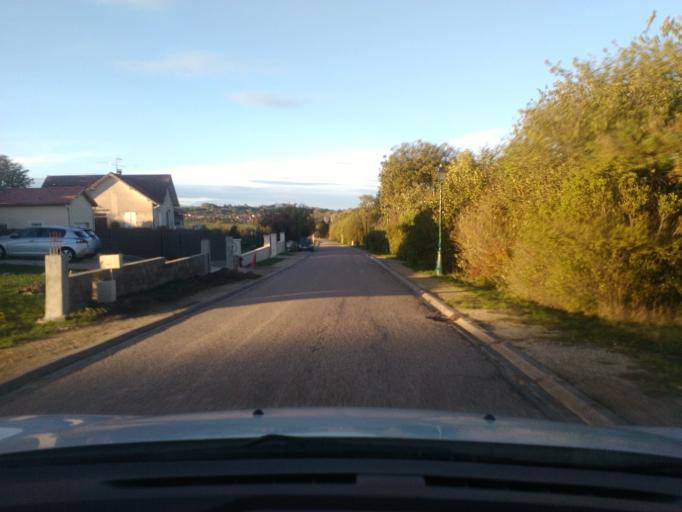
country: FR
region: Lorraine
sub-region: Departement des Vosges
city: Charmes
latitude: 48.3502
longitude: 6.2551
